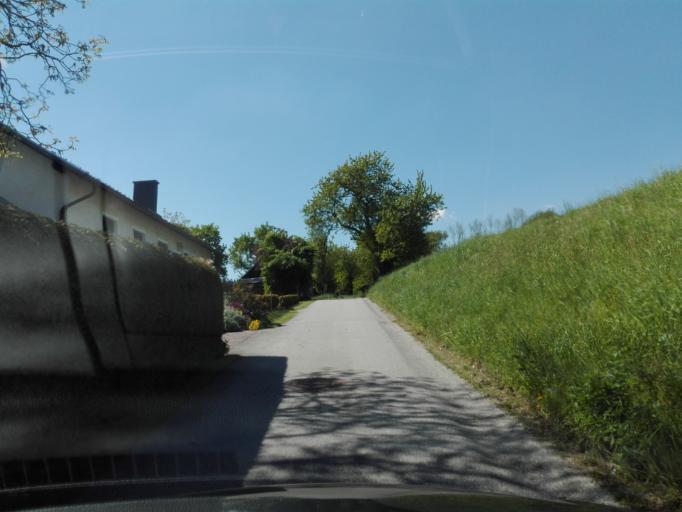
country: AT
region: Upper Austria
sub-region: Politischer Bezirk Urfahr-Umgebung
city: Feldkirchen an der Donau
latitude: 48.3432
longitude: 13.9686
